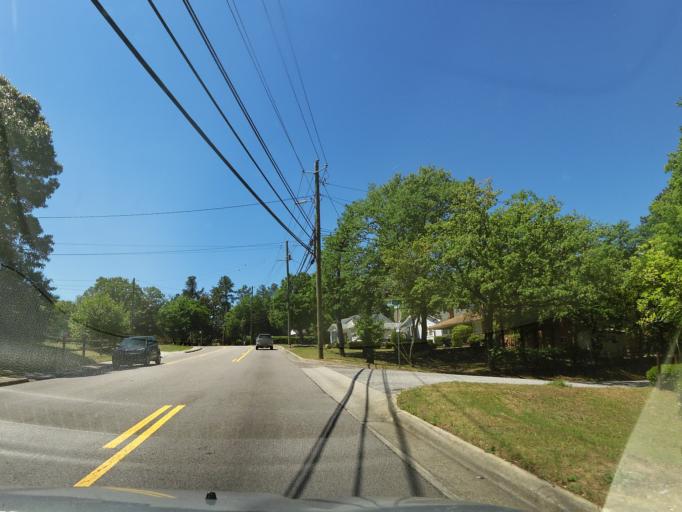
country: US
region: Georgia
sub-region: Columbia County
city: Martinez
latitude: 33.4834
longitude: -82.0304
